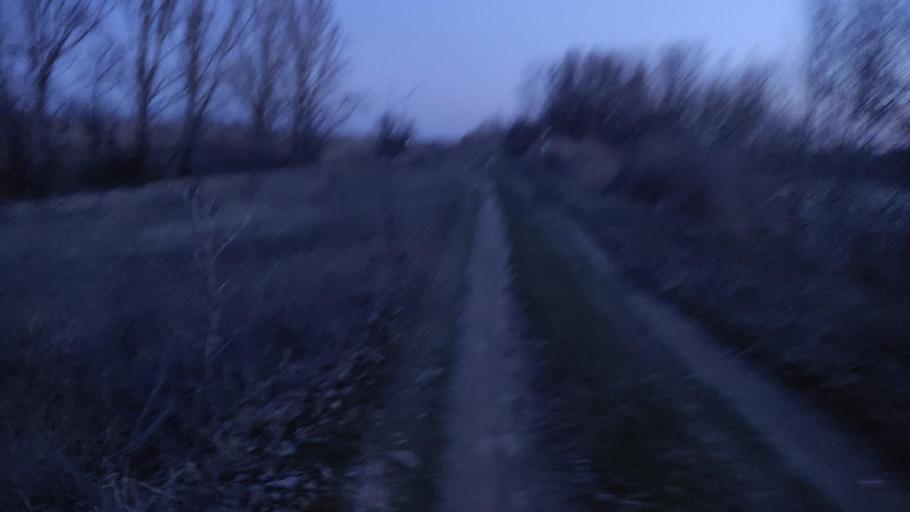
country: MD
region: Bender
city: Bender
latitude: 46.8268
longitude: 29.4943
